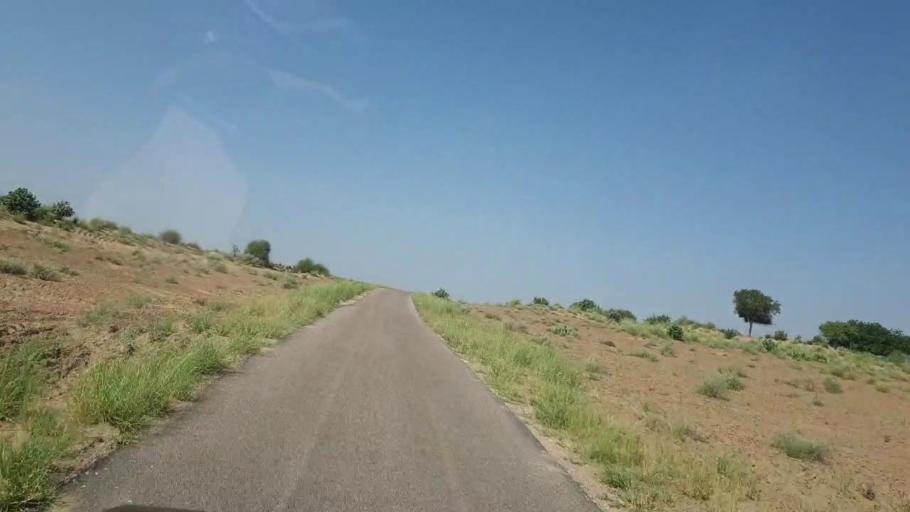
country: PK
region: Sindh
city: Chor
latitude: 25.6334
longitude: 70.3175
